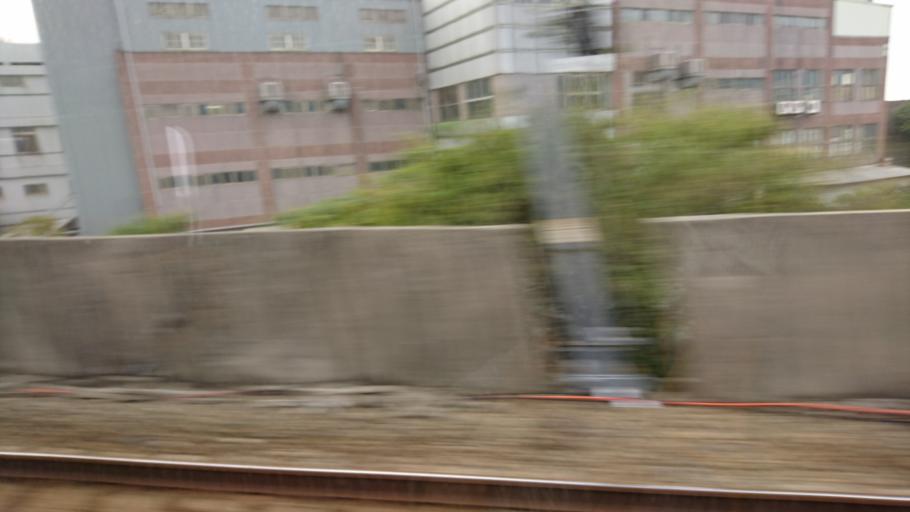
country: TW
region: Taiwan
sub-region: Hsinchu
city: Zhubei
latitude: 24.8490
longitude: 121.0137
